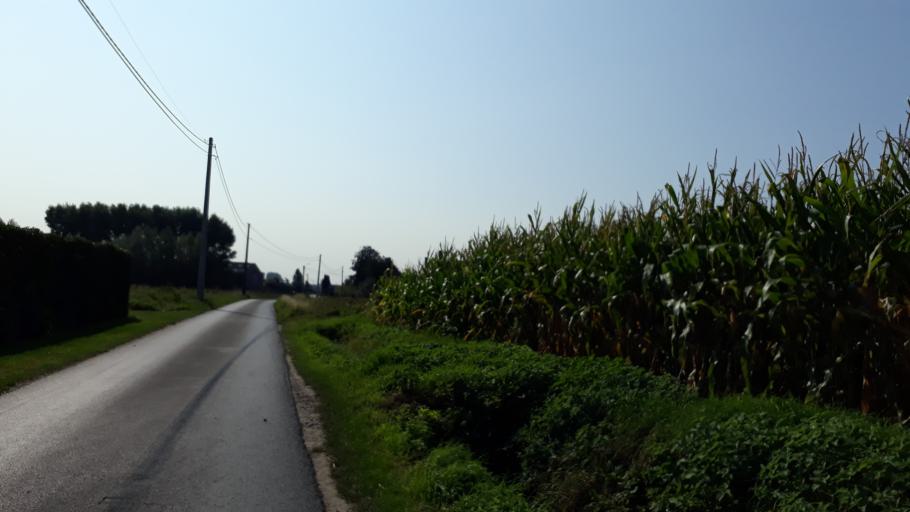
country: BE
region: Flanders
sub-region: Provincie West-Vlaanderen
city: Hooglede
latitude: 51.0187
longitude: 3.0852
